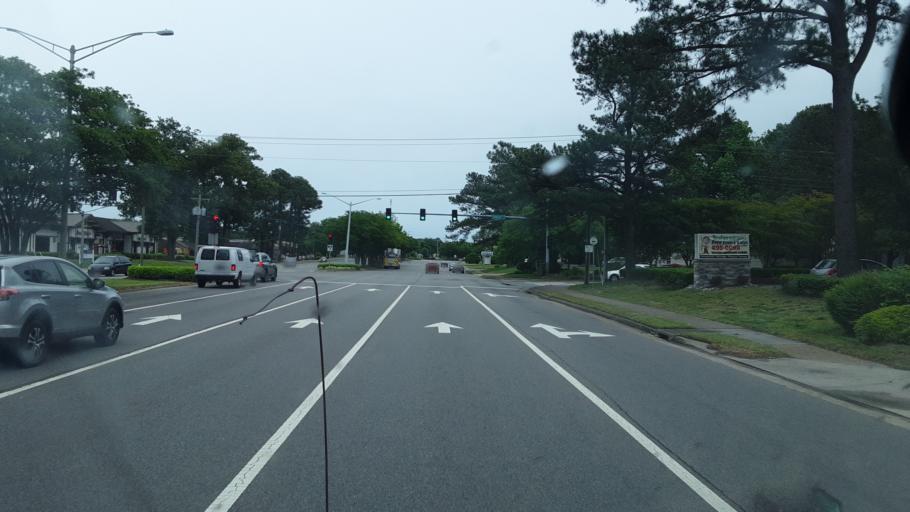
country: US
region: Virginia
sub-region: City of Virginia Beach
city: Virginia Beach
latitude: 36.8433
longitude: -76.1218
